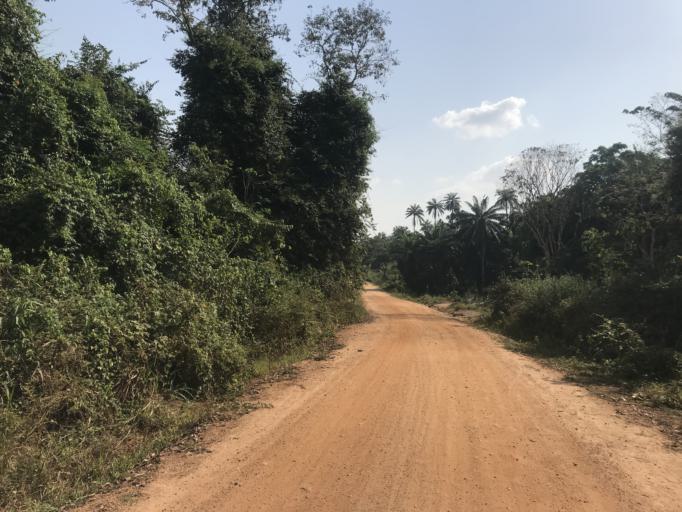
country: NG
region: Osun
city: Ikirun
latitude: 7.8824
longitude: 4.5862
